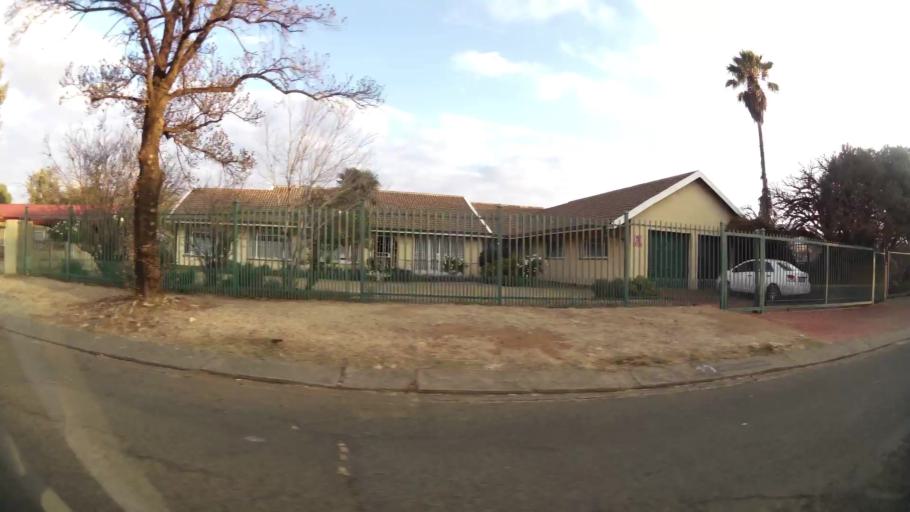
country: ZA
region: Orange Free State
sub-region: Mangaung Metropolitan Municipality
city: Bloemfontein
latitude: -29.1469
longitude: 26.1766
